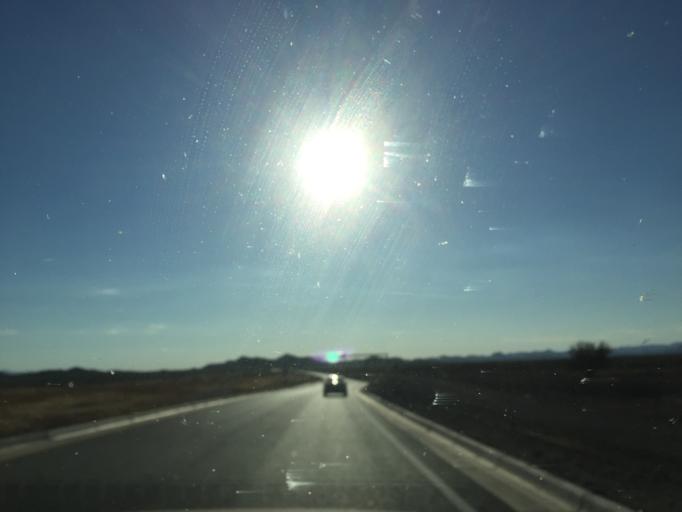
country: US
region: Arizona
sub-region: Maricopa County
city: Anthem
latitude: 33.7696
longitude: -112.1479
